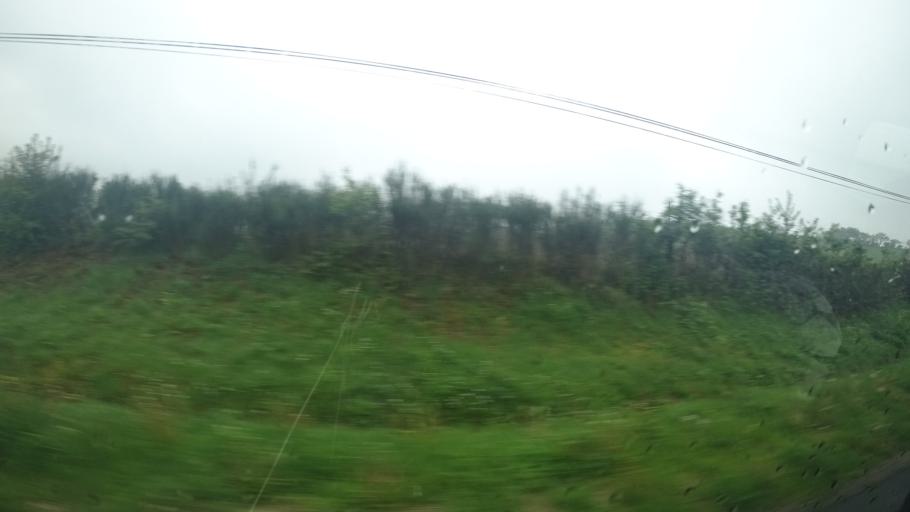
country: FR
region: Midi-Pyrenees
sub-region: Departement de l'Aveyron
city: Laissac
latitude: 44.2807
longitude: 2.8593
